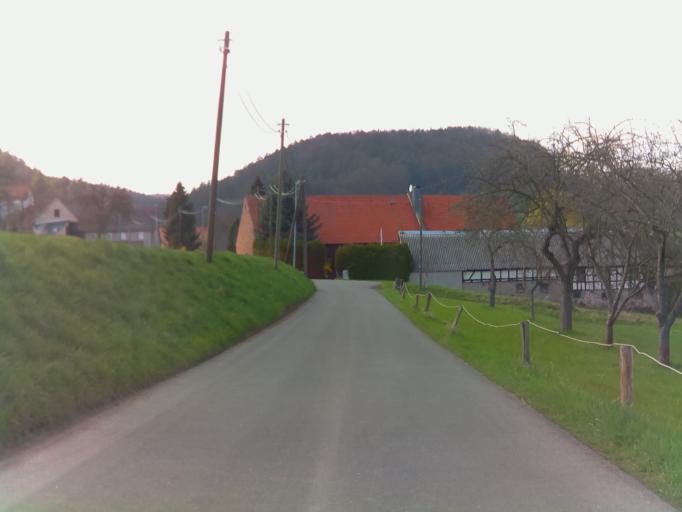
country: DE
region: Thuringia
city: Bibra
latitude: 50.8232
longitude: 11.5604
